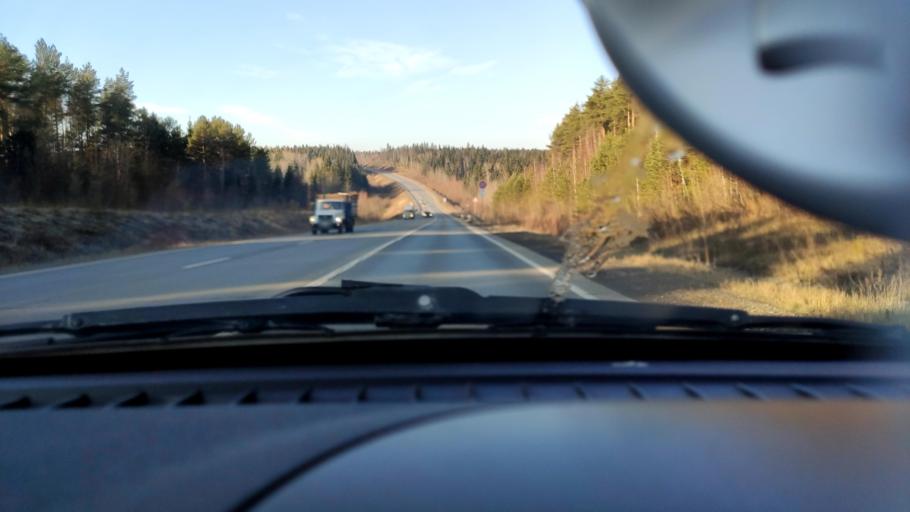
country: RU
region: Perm
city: Novyye Lyady
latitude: 58.0359
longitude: 56.4728
